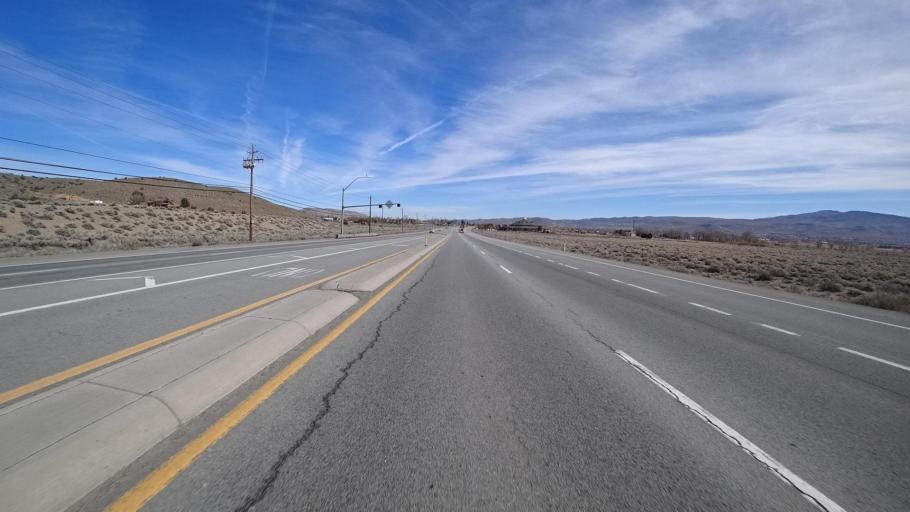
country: US
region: Nevada
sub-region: Washoe County
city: Spanish Springs
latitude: 39.6171
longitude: -119.7278
